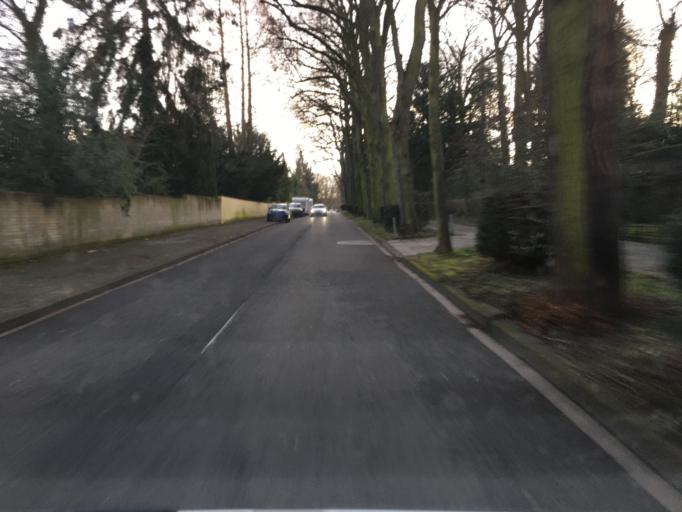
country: DE
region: North Rhine-Westphalia
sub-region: Regierungsbezirk Koln
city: Neustadt/Sued
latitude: 50.9198
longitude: 6.8997
